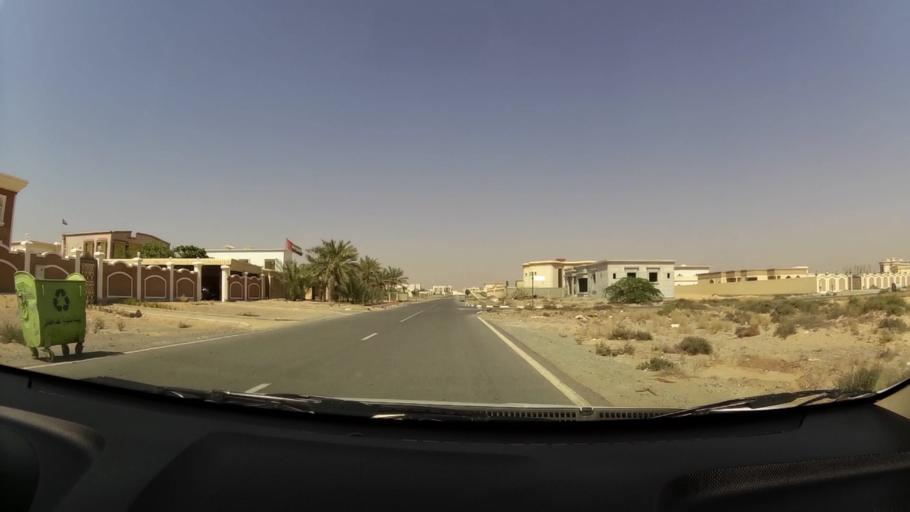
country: AE
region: Umm al Qaywayn
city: Umm al Qaywayn
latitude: 25.4891
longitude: 55.5987
